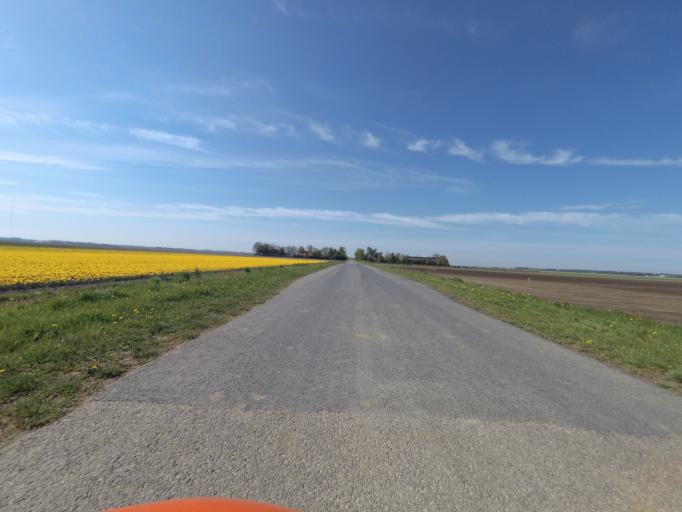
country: NL
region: Flevoland
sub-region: Gemeente Dronten
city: Dronten
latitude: 52.5762
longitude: 5.6994
